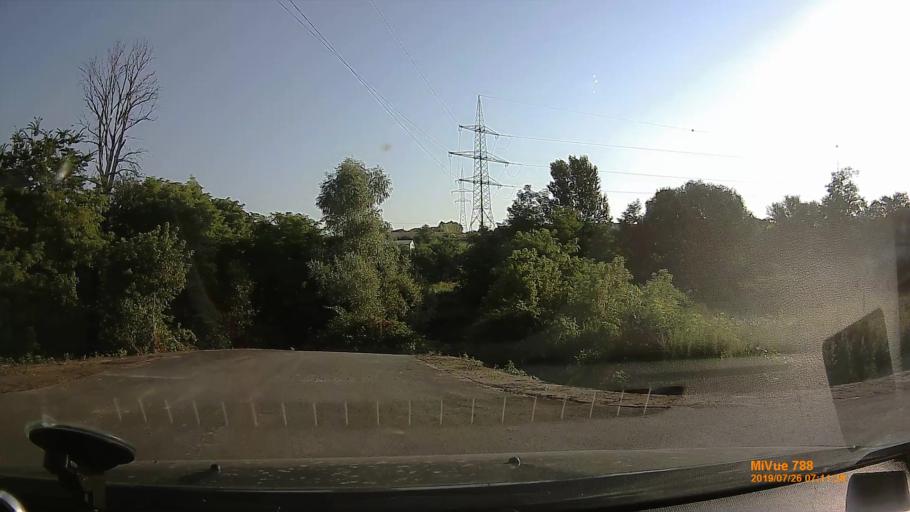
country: HU
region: Pest
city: Mogyorod
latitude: 47.5956
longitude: 19.2239
